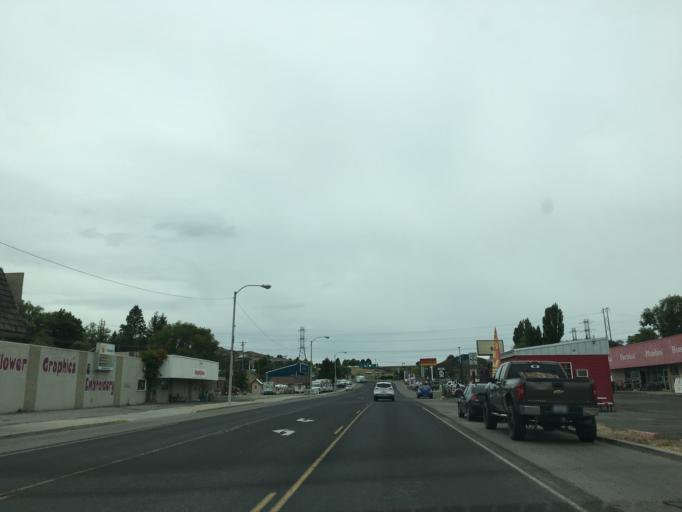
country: US
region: Washington
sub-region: Okanogan County
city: Coulee Dam
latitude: 47.9410
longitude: -119.0064
